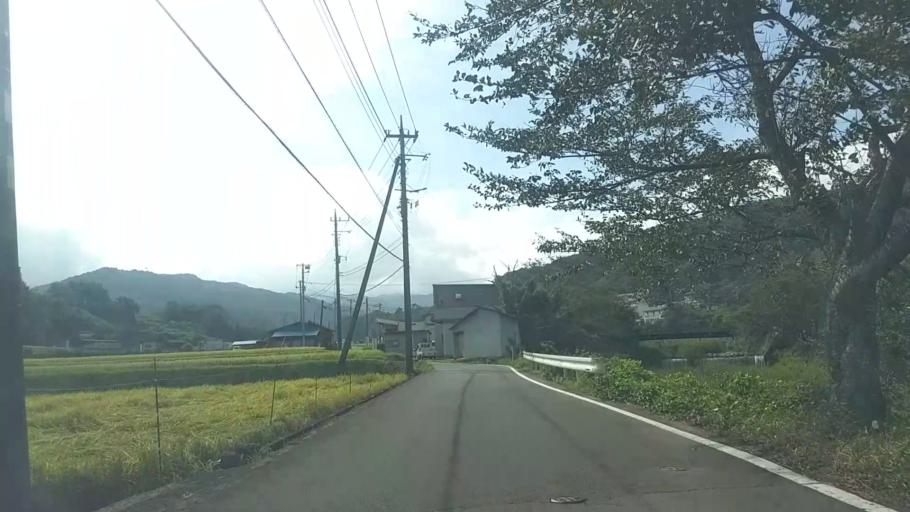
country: JP
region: Shizuoka
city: Heda
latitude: 34.9694
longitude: 138.9139
